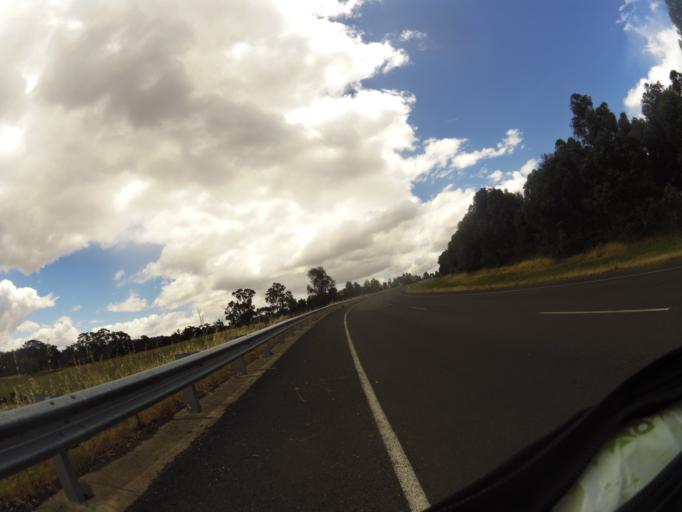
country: AU
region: Victoria
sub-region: Mount Alexander
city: Castlemaine
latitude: -37.0113
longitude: 144.2507
